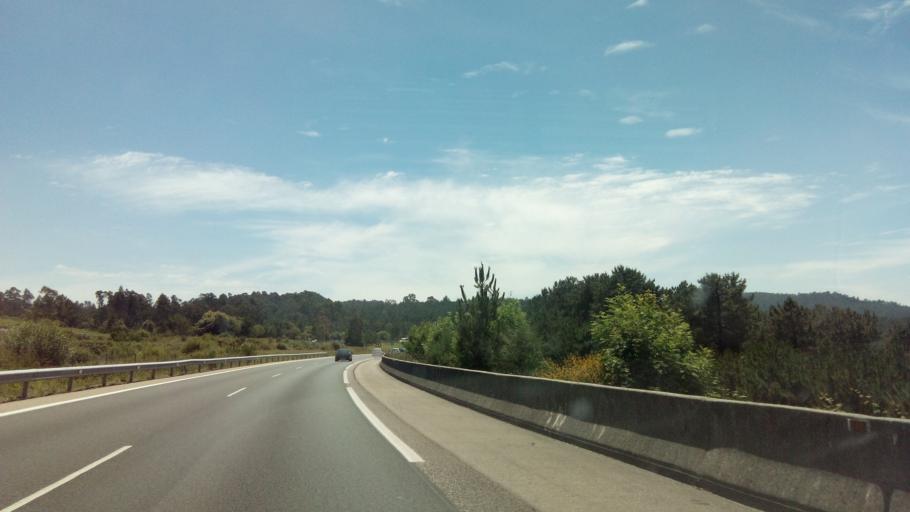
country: ES
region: Galicia
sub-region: Provincia de Pontevedra
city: Porrino
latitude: 42.1967
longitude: -8.6674
